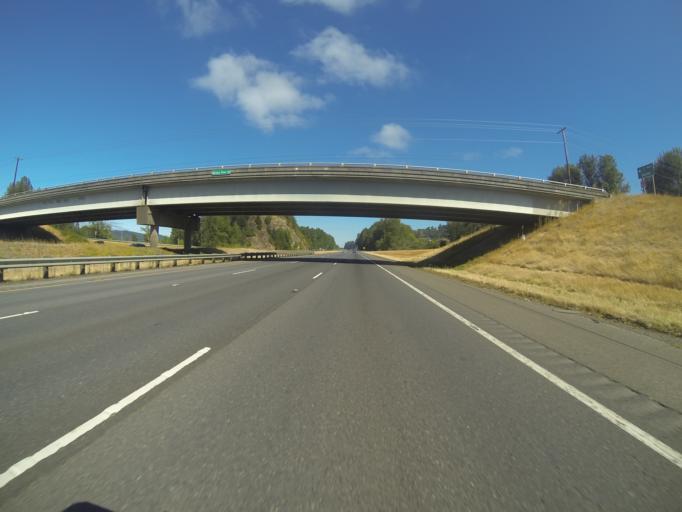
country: US
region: Washington
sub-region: Cowlitz County
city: Kalama
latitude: 46.0411
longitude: -122.8587
